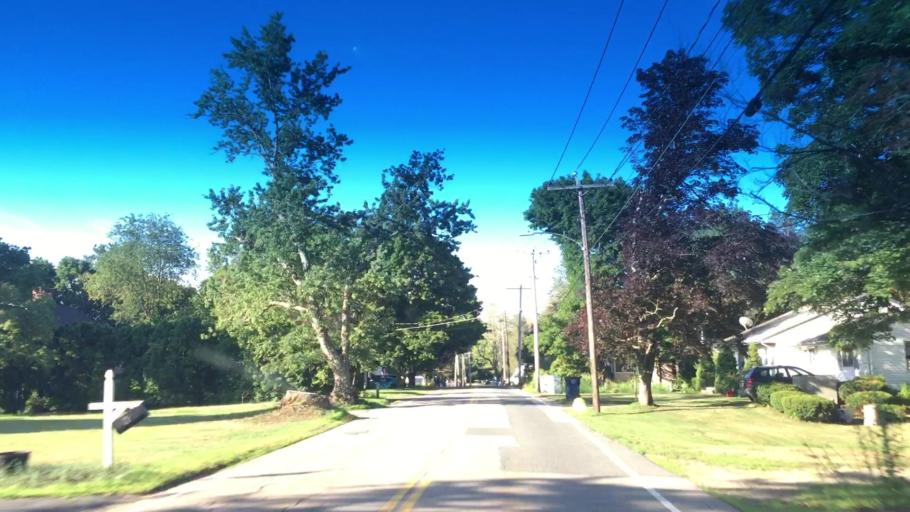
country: US
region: Massachusetts
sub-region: Norfolk County
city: Medway
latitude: 42.1460
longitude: -71.3912
